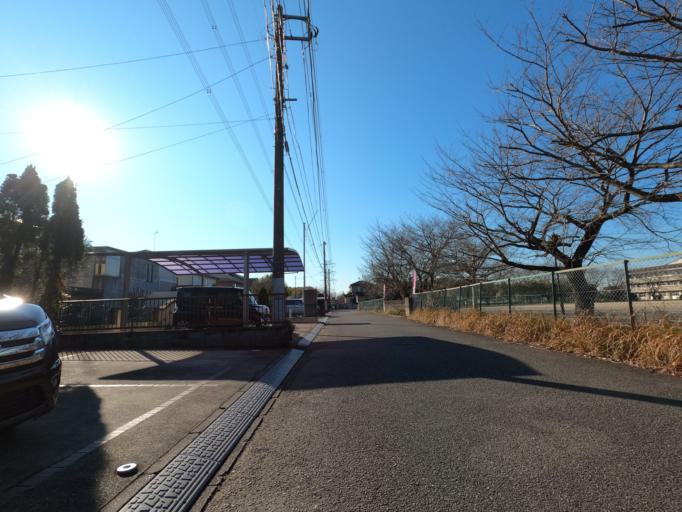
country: JP
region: Ibaraki
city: Moriya
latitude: 35.9622
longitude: 139.9759
